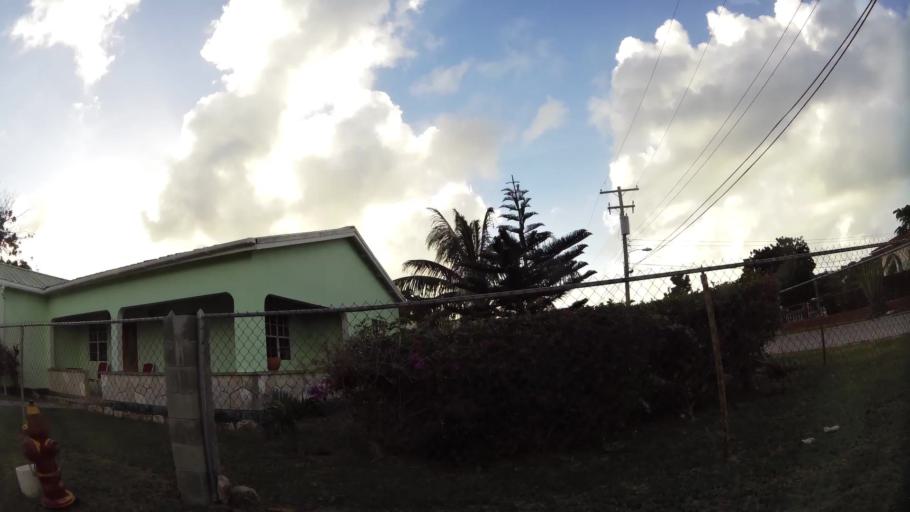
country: AG
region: Saint John
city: Saint John's
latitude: 17.1581
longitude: -61.8229
